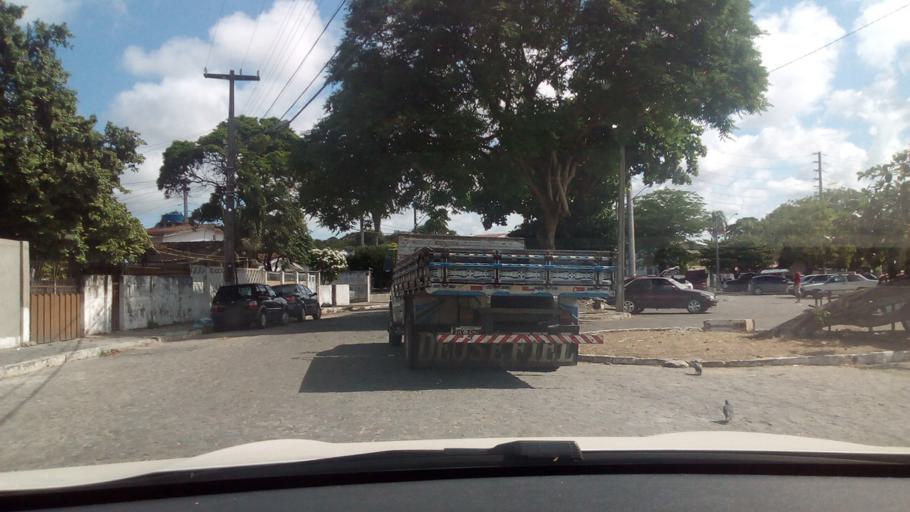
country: BR
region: Paraiba
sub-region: Joao Pessoa
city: Joao Pessoa
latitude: -7.1345
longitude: -34.8712
